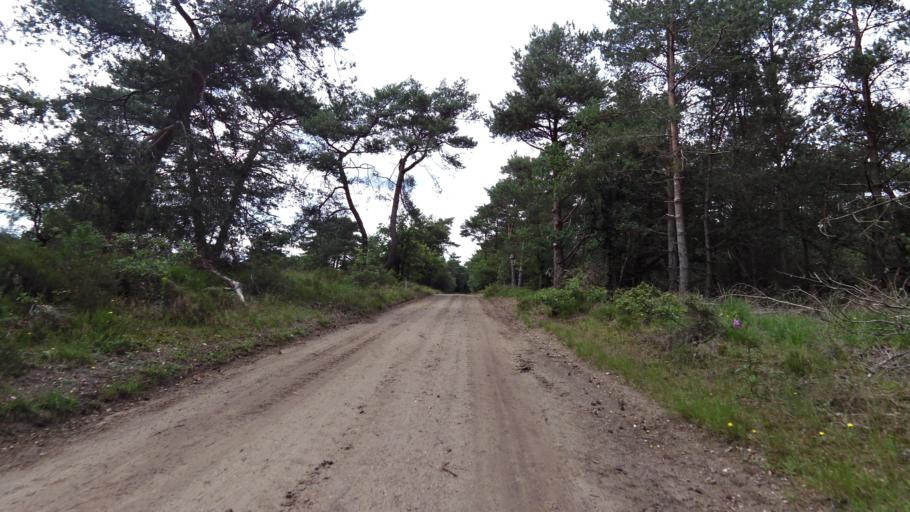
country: NL
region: Gelderland
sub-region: Gemeente Apeldoorn
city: Apeldoorn
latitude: 52.2070
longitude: 5.8721
